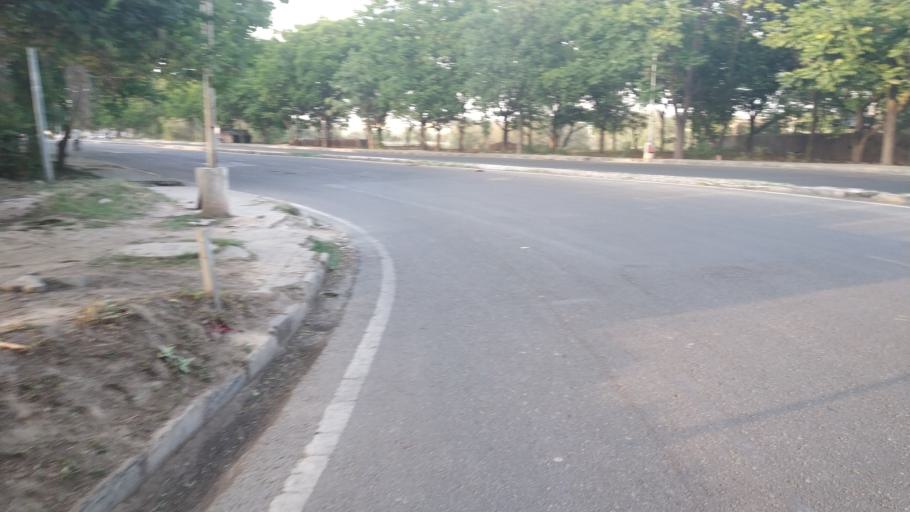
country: IN
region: Punjab
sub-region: Ajitgarh
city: Mohali
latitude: 30.6853
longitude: 76.7312
